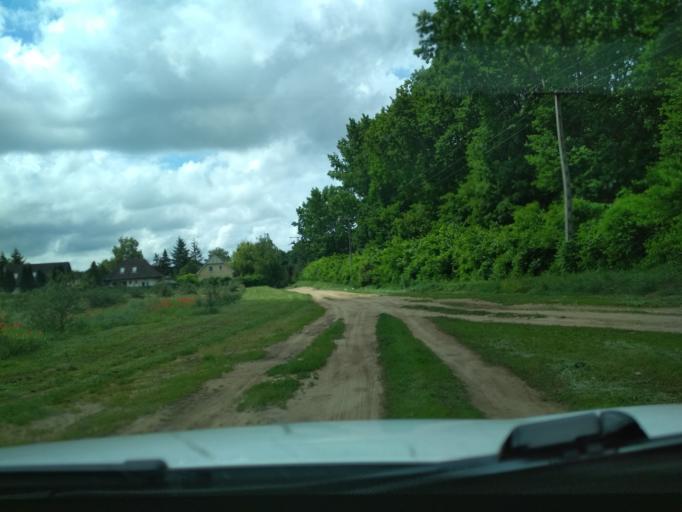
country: HU
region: Jasz-Nagykun-Szolnok
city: Tiszafured
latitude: 47.6204
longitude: 20.7334
